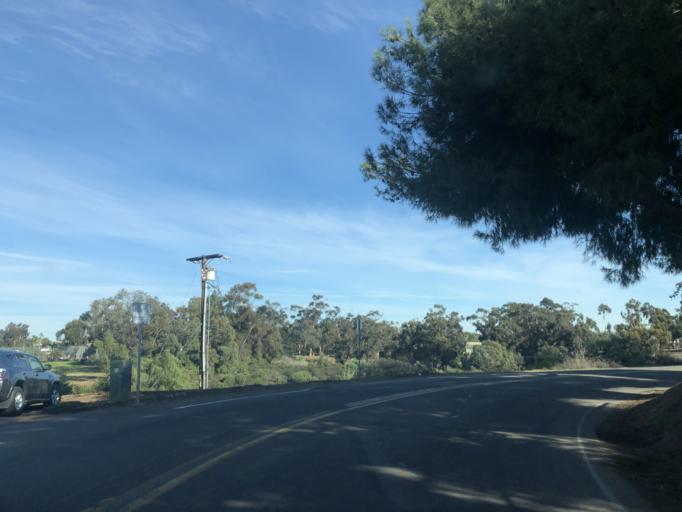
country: US
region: California
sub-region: San Diego County
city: San Diego
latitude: 32.7247
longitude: -117.1373
